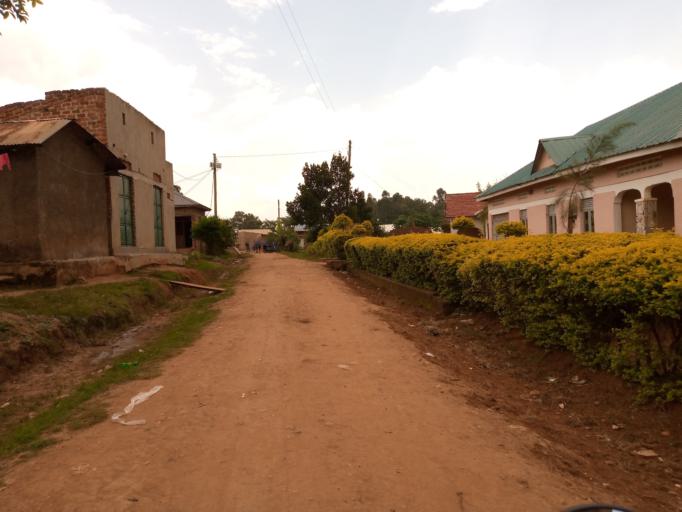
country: UG
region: Eastern Region
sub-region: Mbale District
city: Mbale
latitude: 1.0886
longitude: 34.1653
